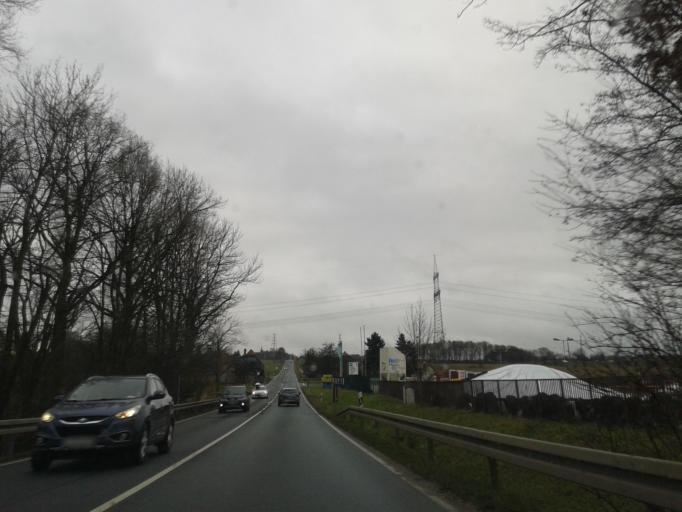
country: DE
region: Saxony
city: Grossschweidnitz
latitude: 51.0518
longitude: 14.6390
